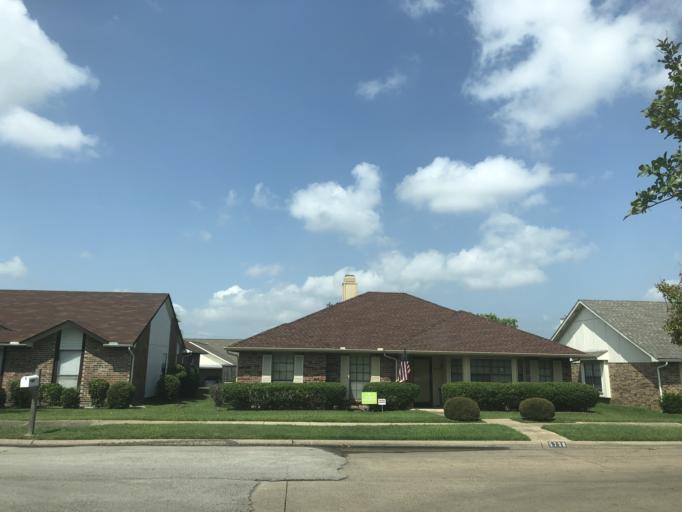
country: US
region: Texas
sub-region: Dallas County
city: Sunnyvale
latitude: 32.8359
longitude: -96.5638
